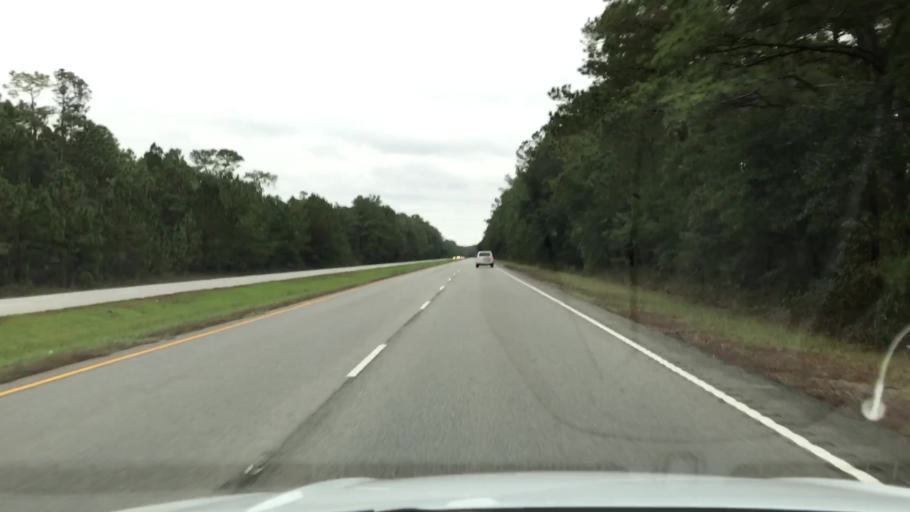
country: US
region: South Carolina
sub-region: Georgetown County
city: Georgetown
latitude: 33.3927
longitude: -79.2029
